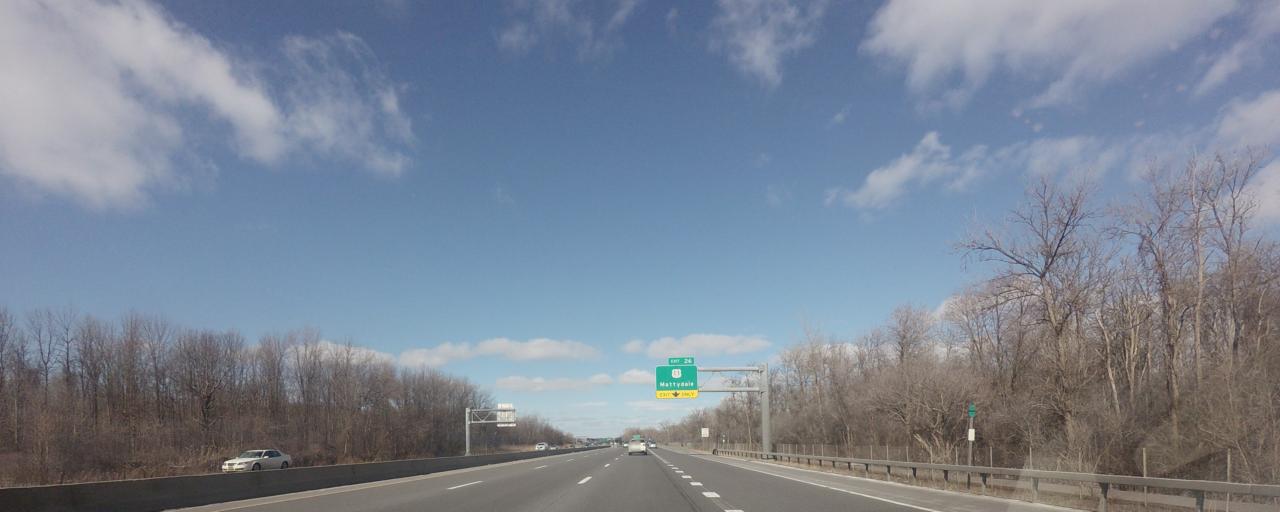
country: US
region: New York
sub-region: Onondaga County
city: Mattydale
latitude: 43.0993
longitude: -76.1574
